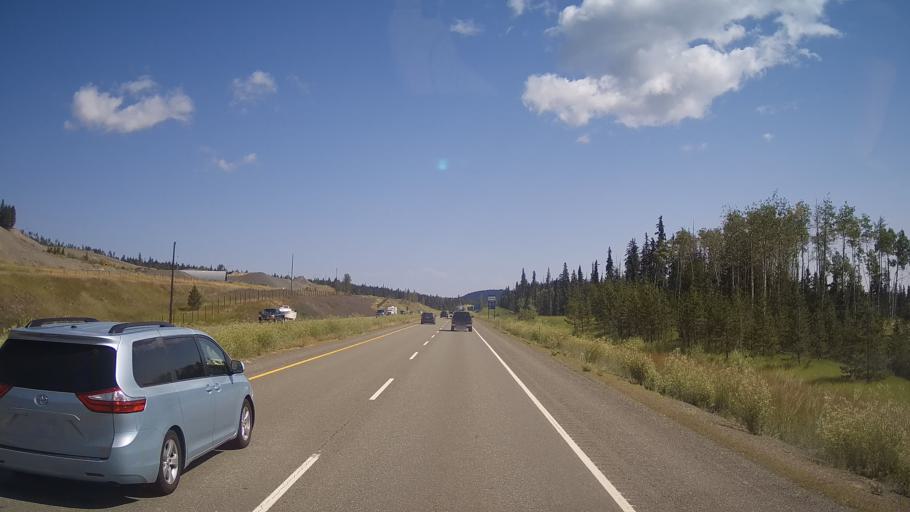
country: CA
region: British Columbia
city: Logan Lake
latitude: 50.4777
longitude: -120.5686
